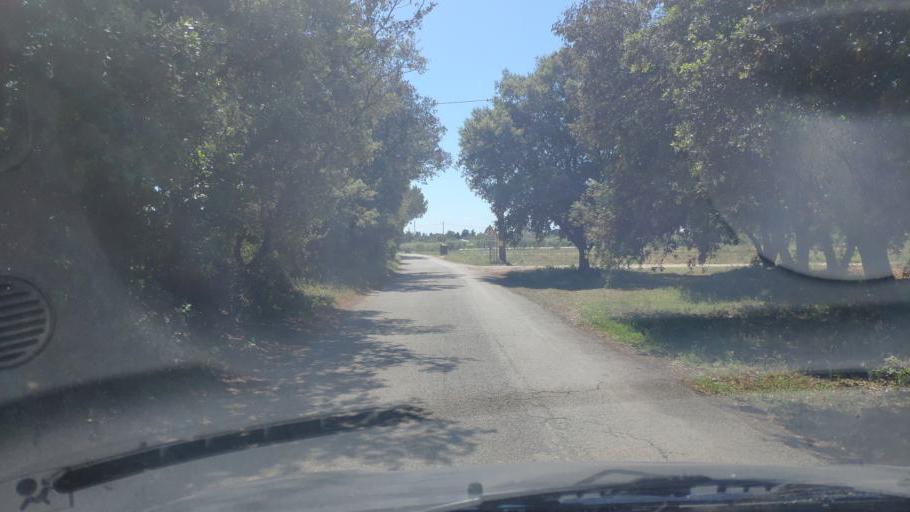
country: FR
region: Provence-Alpes-Cote d'Azur
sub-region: Departement du Vaucluse
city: Carpentras
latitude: 44.0710
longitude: 5.0368
